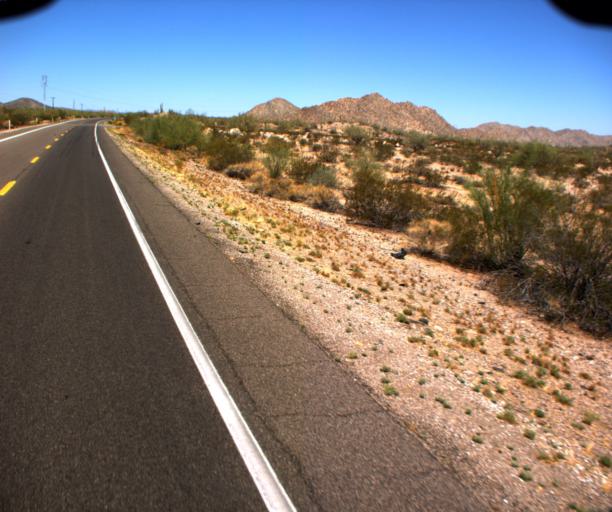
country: US
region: Arizona
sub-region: Pinal County
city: Maricopa
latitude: 32.8437
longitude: -112.1015
